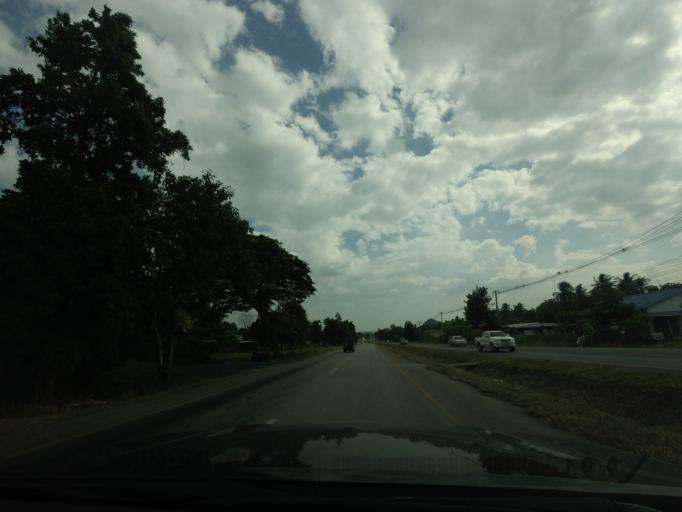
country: TH
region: Lop Buri
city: Chai Badan
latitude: 15.2423
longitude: 101.1261
